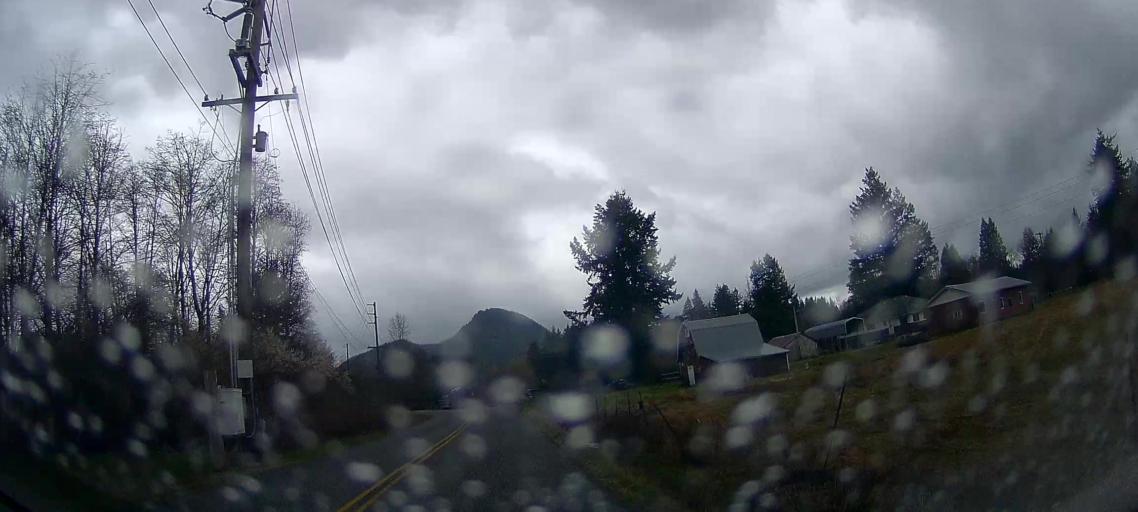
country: US
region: Washington
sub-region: Whatcom County
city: Sudden Valley
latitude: 48.6117
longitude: -122.3363
